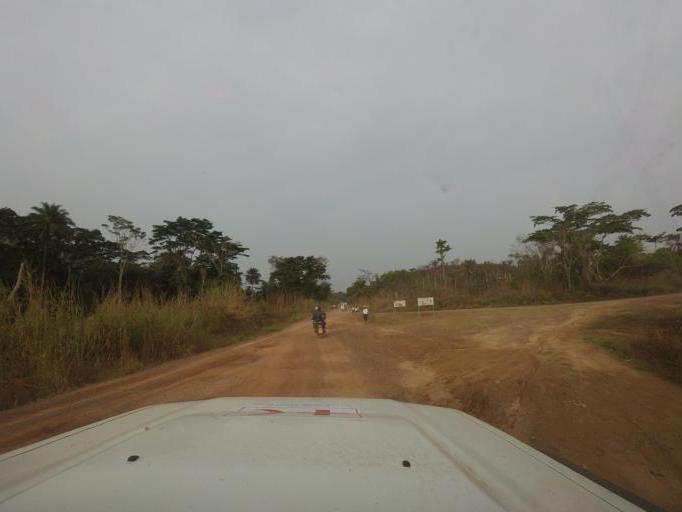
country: LR
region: Lofa
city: Voinjama
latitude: 8.3692
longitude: -9.9075
